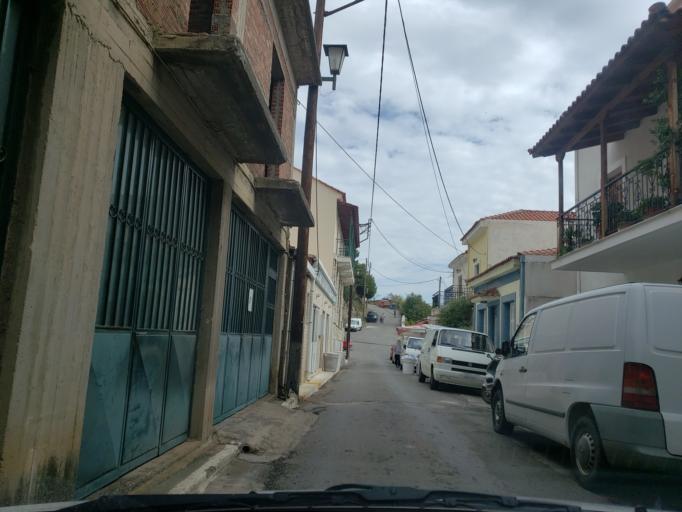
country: GR
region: Central Greece
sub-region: Nomos Fokidos
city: Delphi
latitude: 38.4792
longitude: 22.4960
